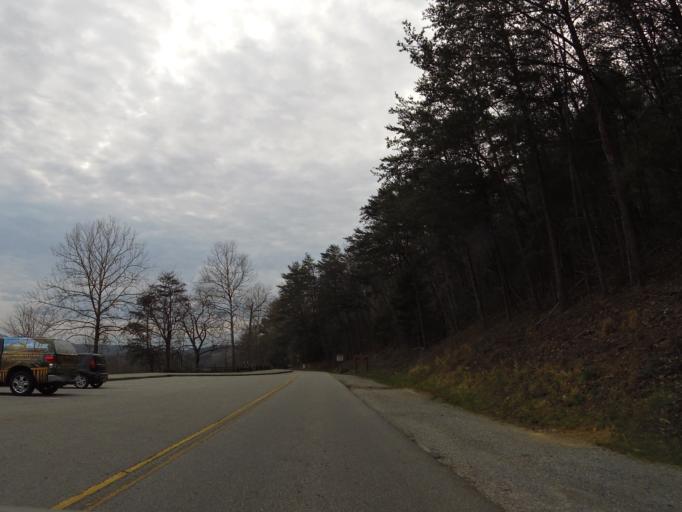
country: US
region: Tennessee
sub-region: Blount County
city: Wildwood
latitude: 35.6066
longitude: -83.7771
